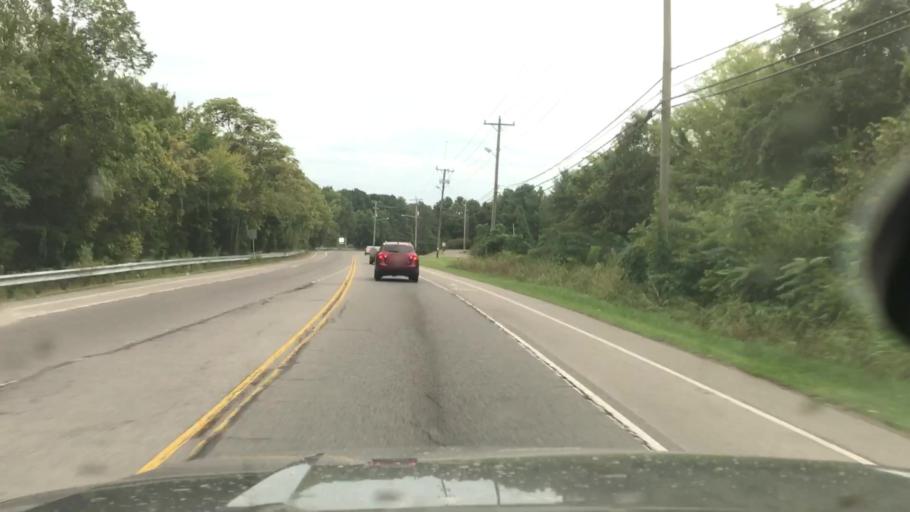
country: US
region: Tennessee
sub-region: Davidson County
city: Lakewood
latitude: 36.1342
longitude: -86.6299
